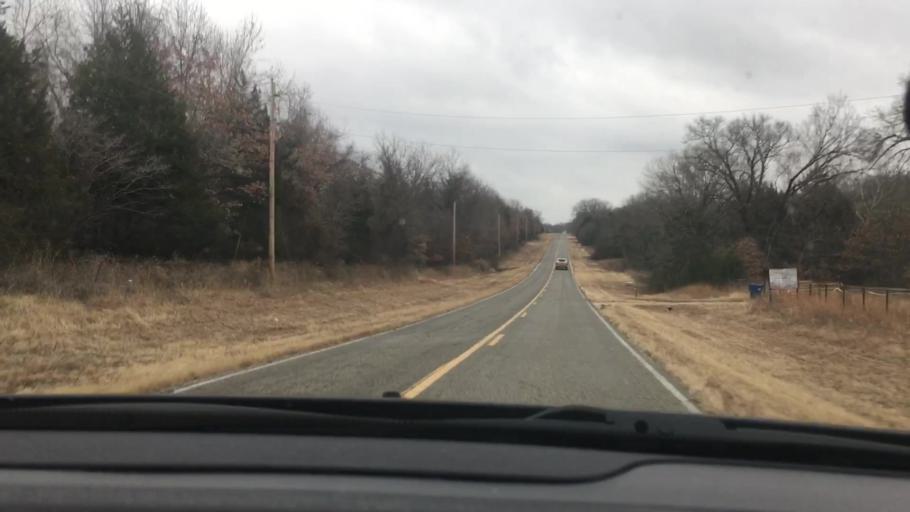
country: US
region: Oklahoma
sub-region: Johnston County
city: Tishomingo
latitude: 34.2087
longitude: -96.5984
